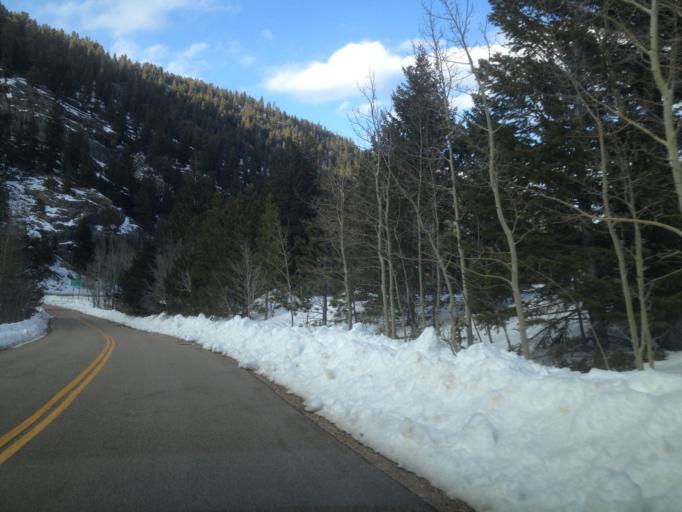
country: US
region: Colorado
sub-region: Boulder County
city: Nederland
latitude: 40.1354
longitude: -105.4921
